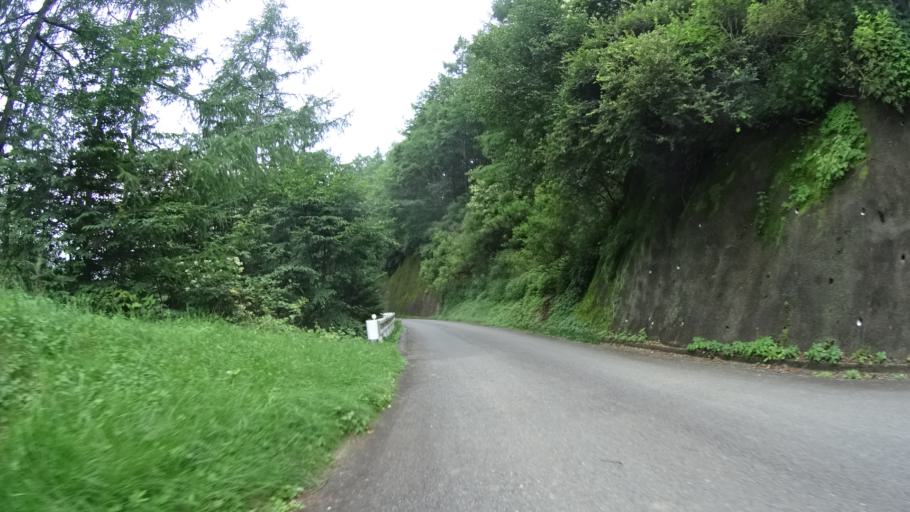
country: JP
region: Nagano
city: Saku
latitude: 36.0967
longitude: 138.6781
